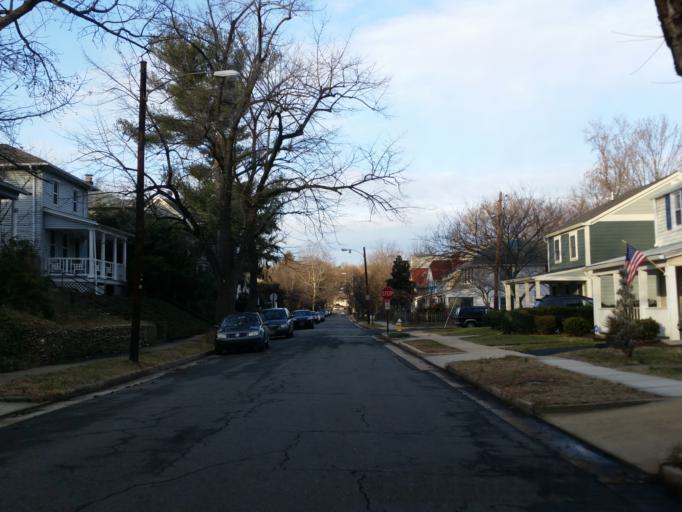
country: US
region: Virginia
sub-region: City of Alexandria
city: Alexandria
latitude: 38.8110
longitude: -77.0578
